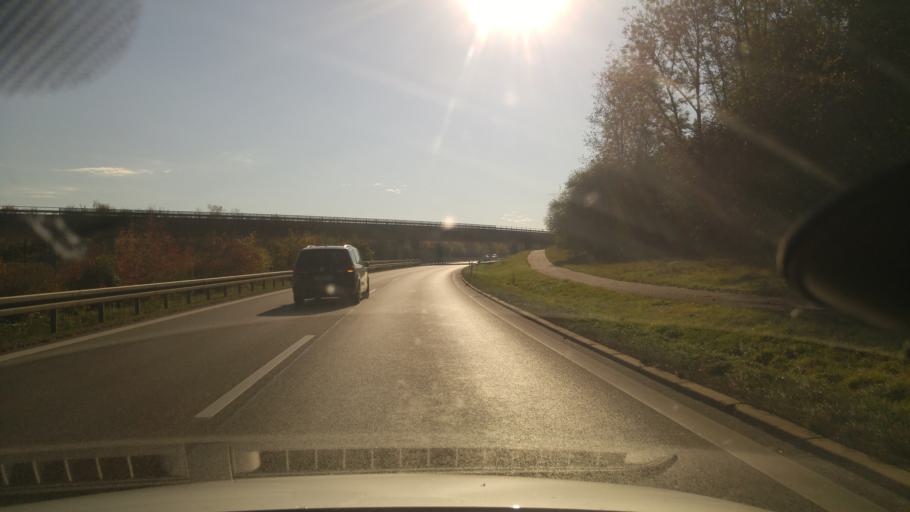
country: DE
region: Baden-Wuerttemberg
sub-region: Regierungsbezirk Stuttgart
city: Plochingen
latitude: 48.7044
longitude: 9.4138
